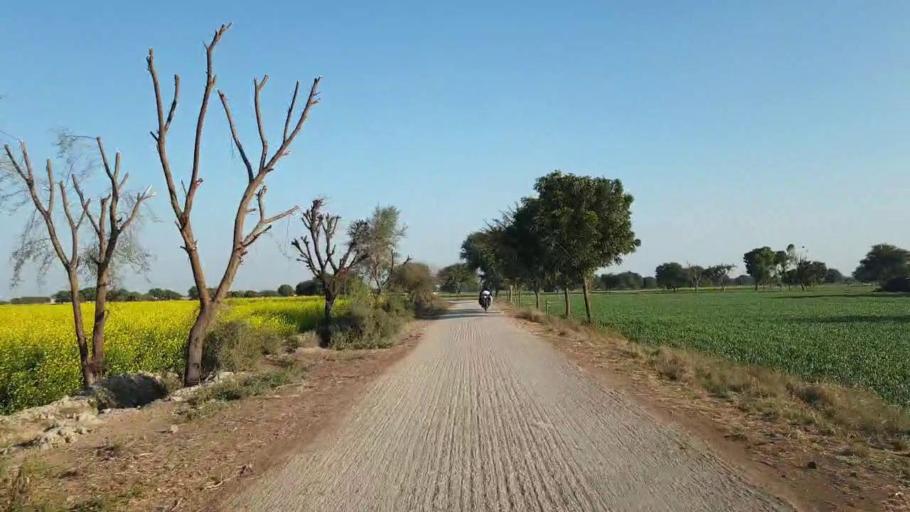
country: PK
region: Sindh
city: Shahpur Chakar
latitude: 26.1282
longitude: 68.5528
